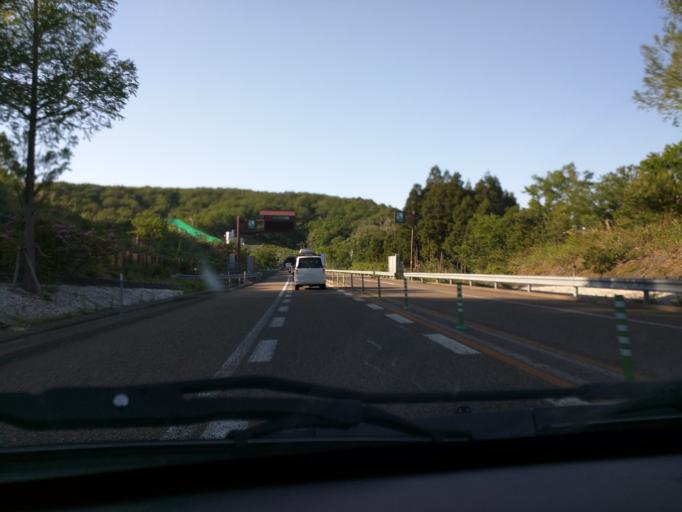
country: JP
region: Niigata
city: Arai
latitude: 37.0401
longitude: 138.2321
